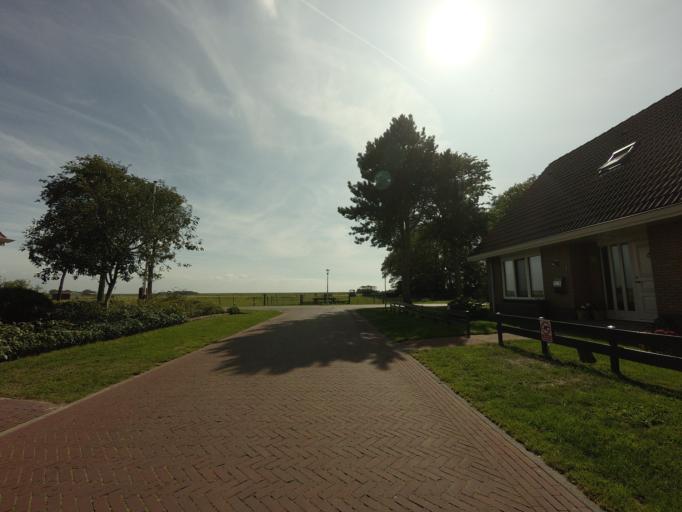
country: NL
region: Friesland
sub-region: Gemeente Ameland
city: Hollum
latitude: 53.4422
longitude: 5.6897
